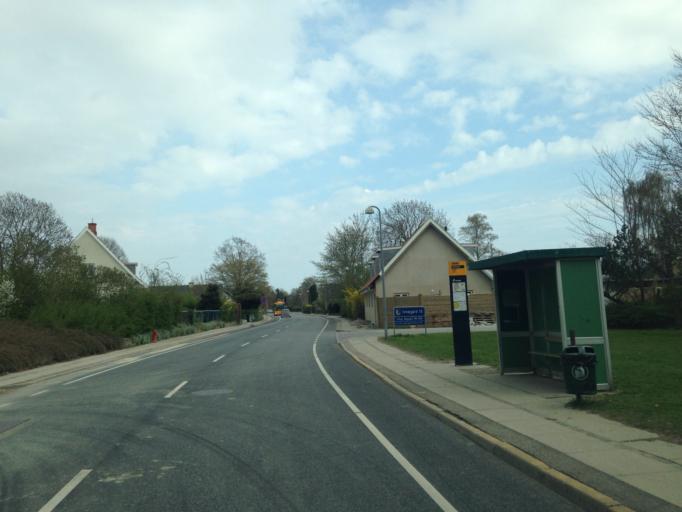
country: DK
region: Capital Region
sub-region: Hoje-Taastrup Kommune
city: Taastrup
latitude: 55.6250
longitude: 12.3016
